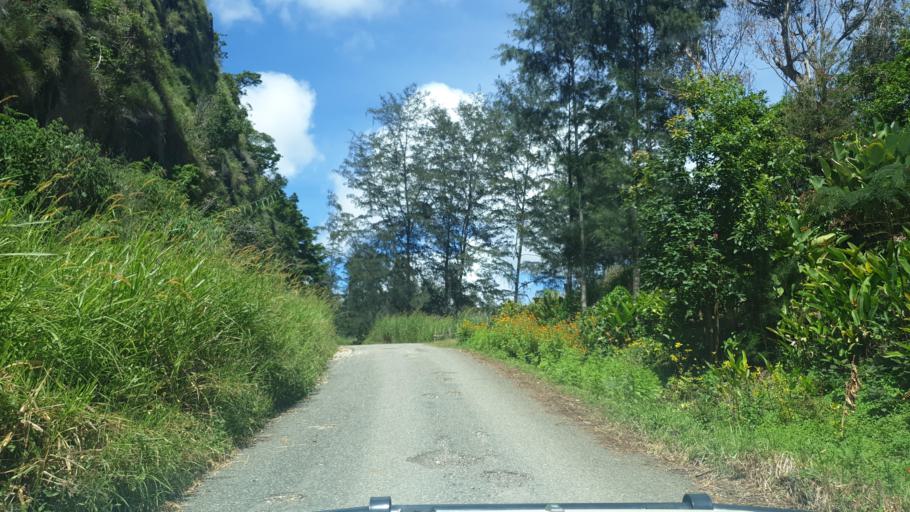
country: PG
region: Chimbu
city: Kundiawa
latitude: -6.1487
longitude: 145.1340
